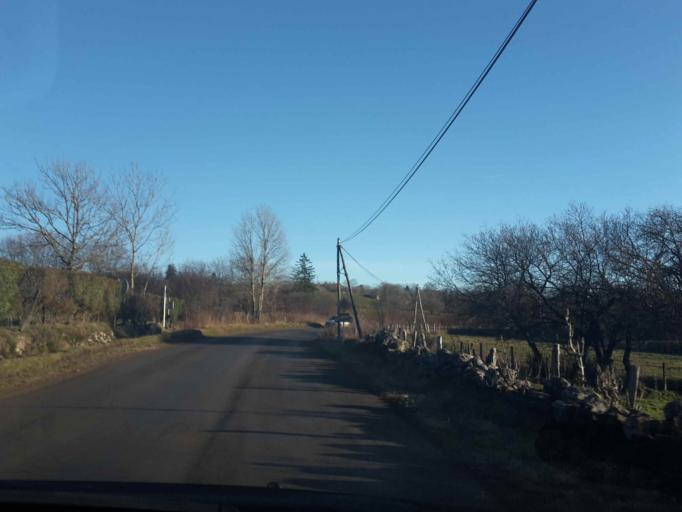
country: FR
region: Auvergne
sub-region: Departement du Cantal
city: Ydes
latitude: 45.2465
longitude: 2.5403
